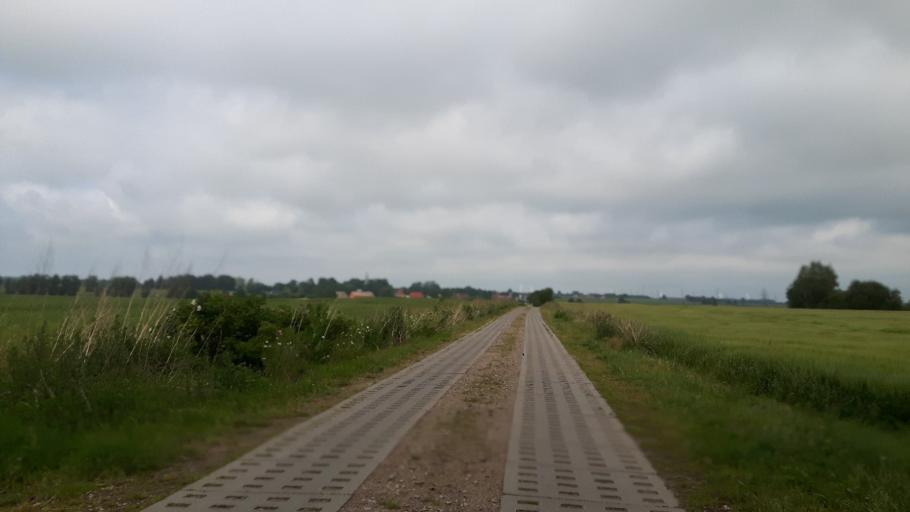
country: PL
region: West Pomeranian Voivodeship
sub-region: Powiat koszalinski
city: Sianow
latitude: 54.2881
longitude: 16.2623
